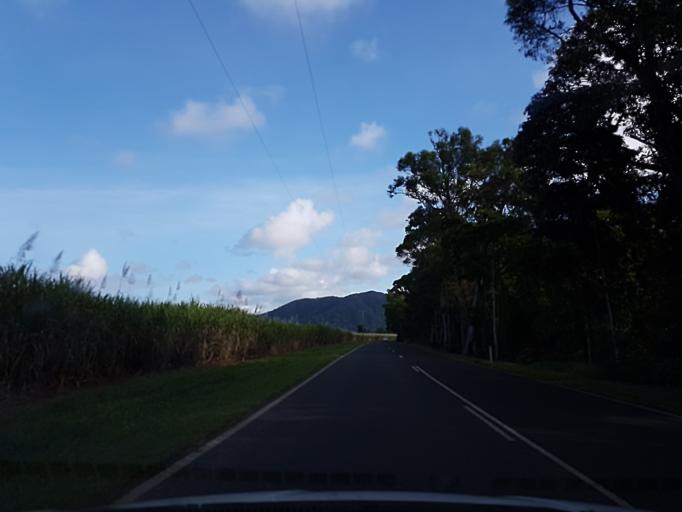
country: AU
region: Queensland
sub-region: Cairns
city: Port Douglas
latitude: -16.2721
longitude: 145.3916
